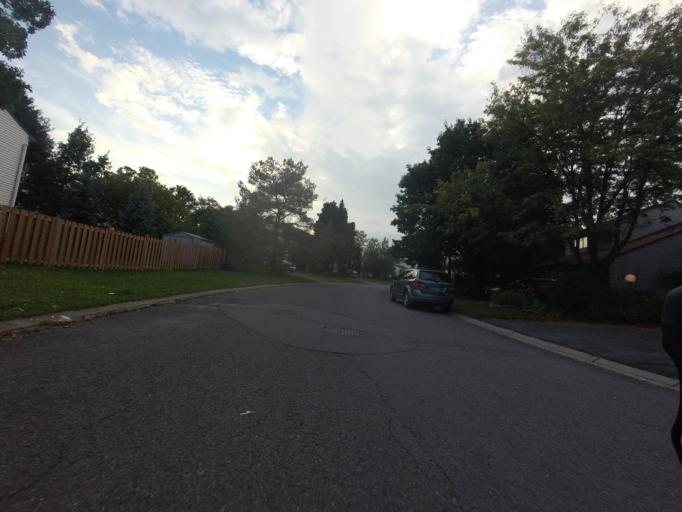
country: CA
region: Ontario
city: Bells Corners
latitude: 45.2700
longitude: -75.7509
